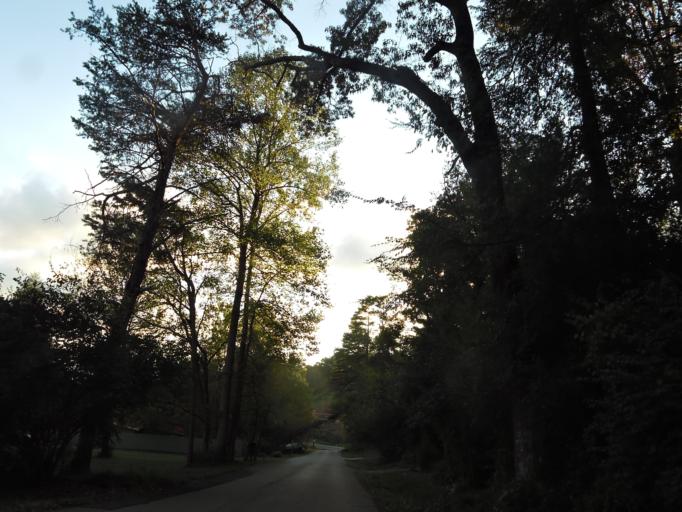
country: US
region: Tennessee
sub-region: Knox County
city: Knoxville
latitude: 35.9175
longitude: -83.9533
